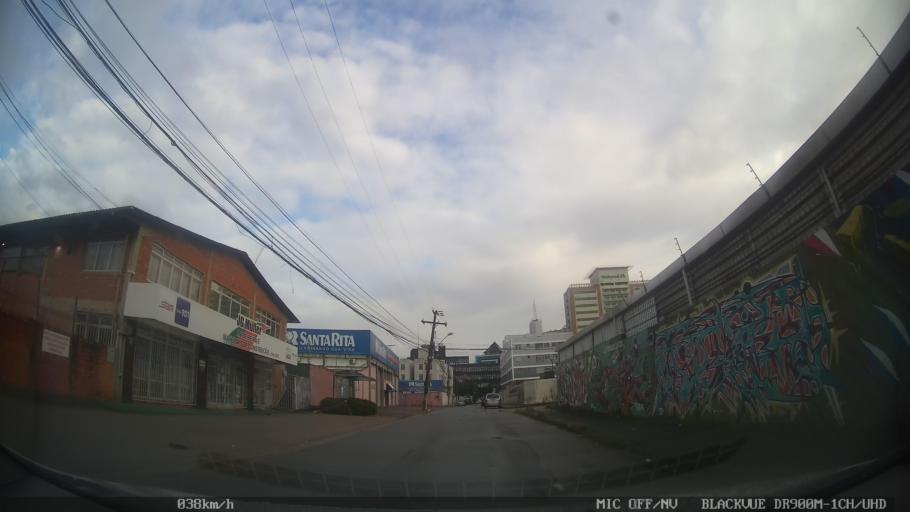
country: BR
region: Santa Catarina
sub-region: Sao Jose
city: Campinas
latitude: -27.5885
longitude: -48.6103
